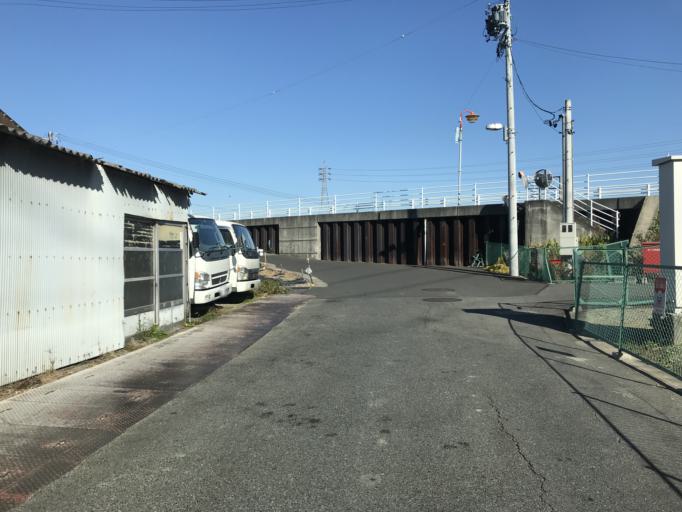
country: JP
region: Aichi
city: Nagoya-shi
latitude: 35.1951
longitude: 136.8386
